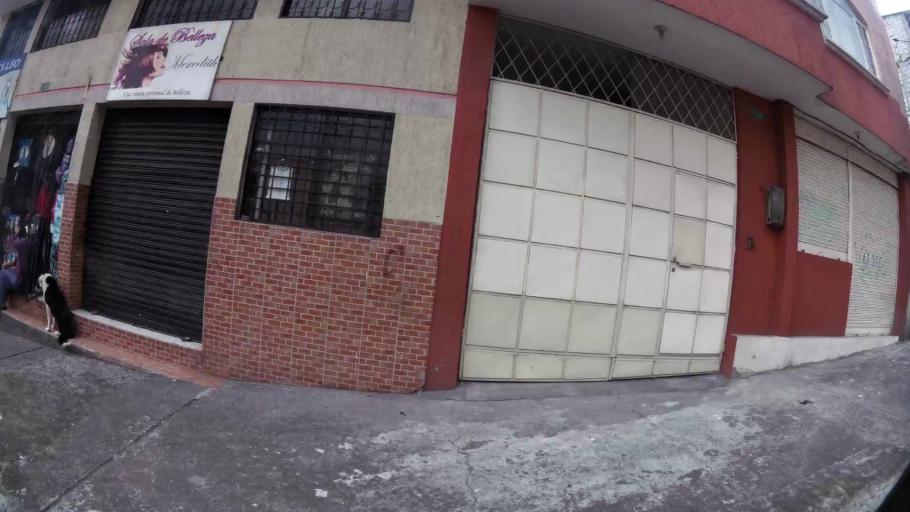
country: EC
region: Pichincha
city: Quito
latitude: -0.2405
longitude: -78.5066
